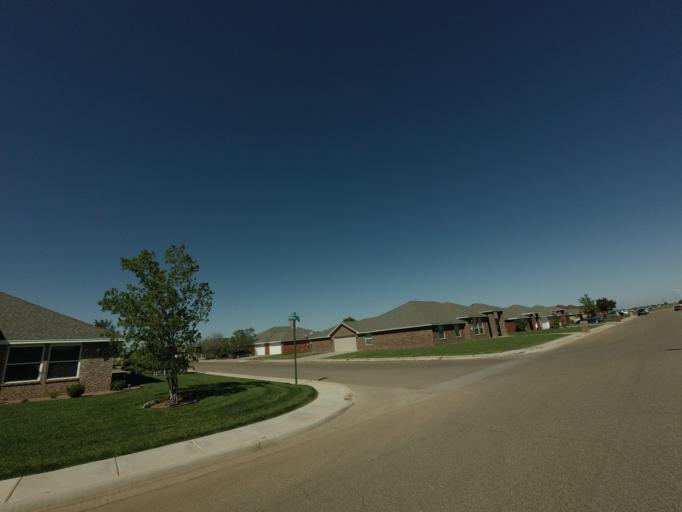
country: US
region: New Mexico
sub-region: Curry County
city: Clovis
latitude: 34.4306
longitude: -103.1691
